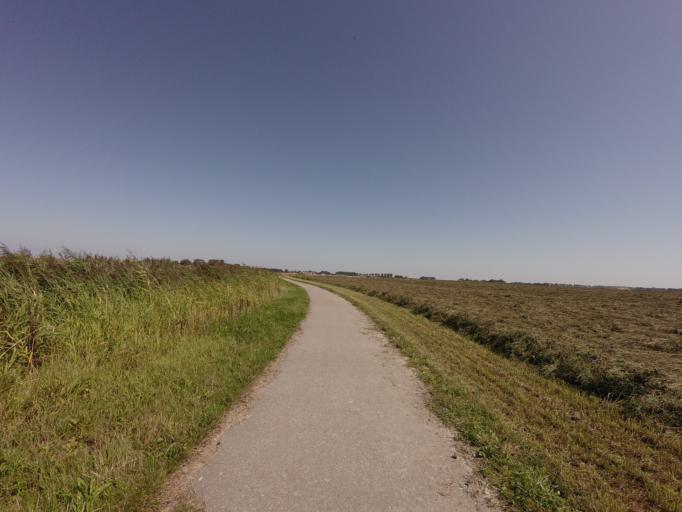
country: NL
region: Friesland
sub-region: Gemeente Dongeradeel
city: Anjum
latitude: 53.3931
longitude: 6.0687
